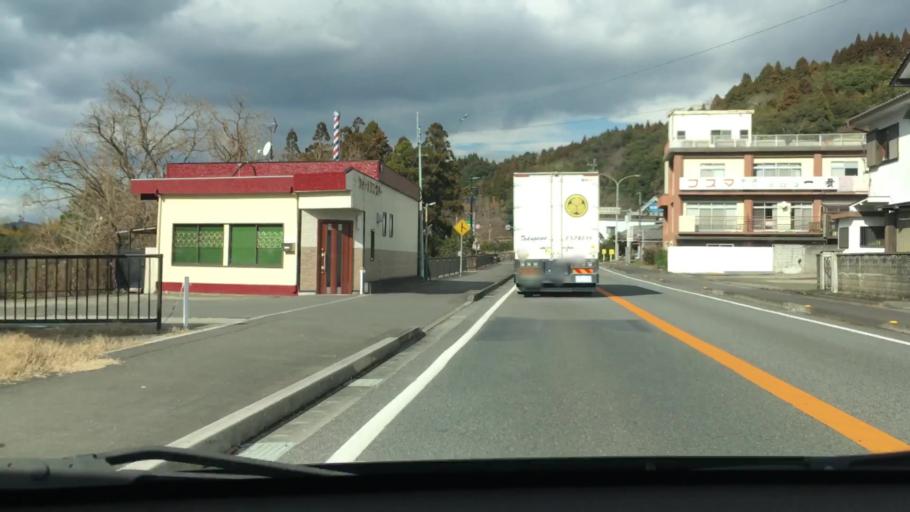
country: JP
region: Oita
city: Usuki
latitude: 33.0455
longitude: 131.6919
